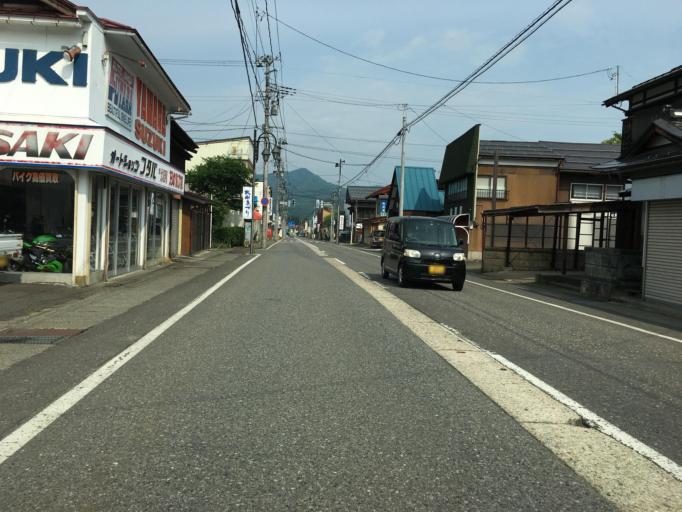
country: JP
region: Fukushima
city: Kitakata
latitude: 37.5853
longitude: 139.6478
